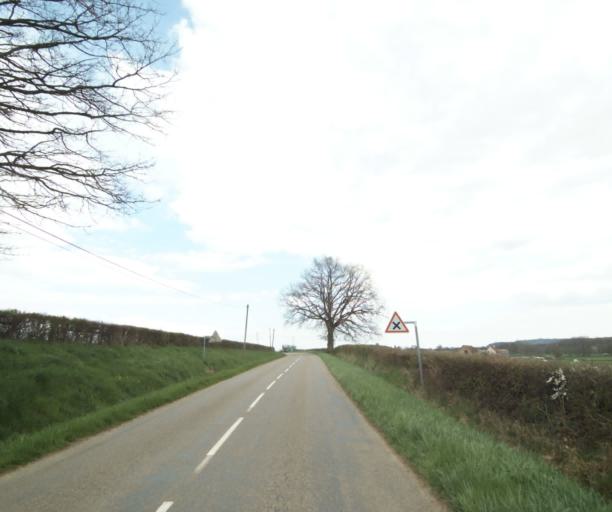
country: FR
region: Bourgogne
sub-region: Departement de Saone-et-Loire
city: Saint-Vallier
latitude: 46.5410
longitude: 4.3760
